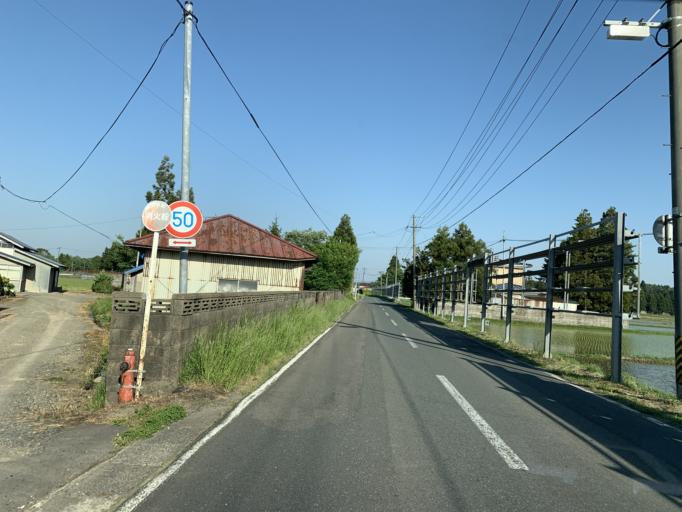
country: JP
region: Iwate
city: Kitakami
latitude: 39.2940
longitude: 140.9888
